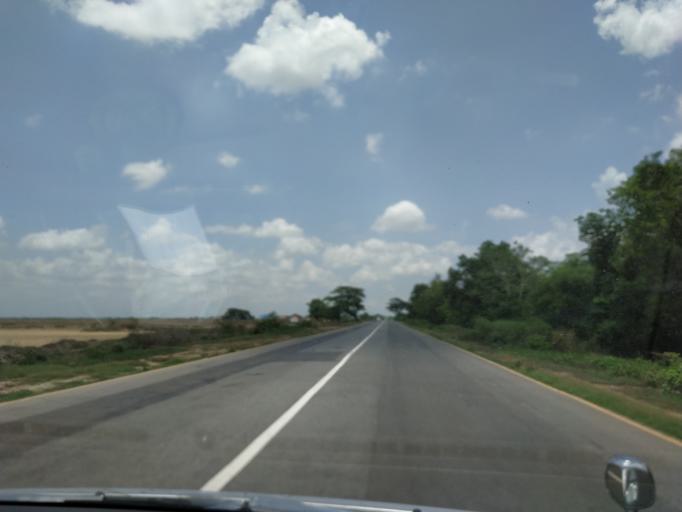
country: MM
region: Bago
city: Bago
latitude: 17.4612
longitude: 96.5963
